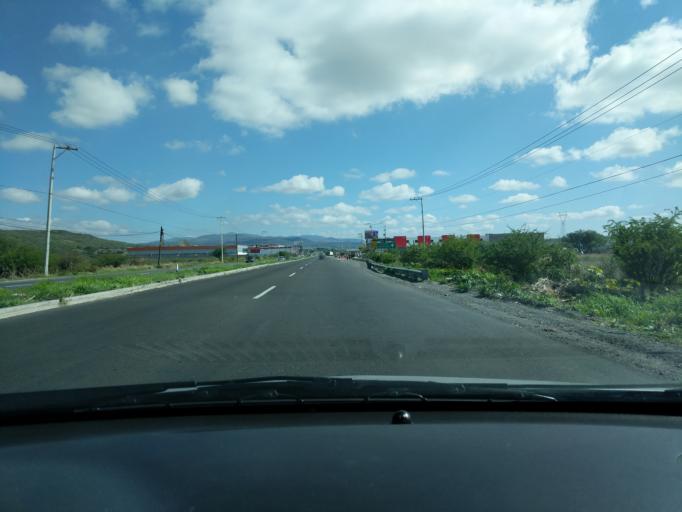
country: MX
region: Queretaro
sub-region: Queretaro
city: Patria Nueva
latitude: 20.6346
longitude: -100.4995
